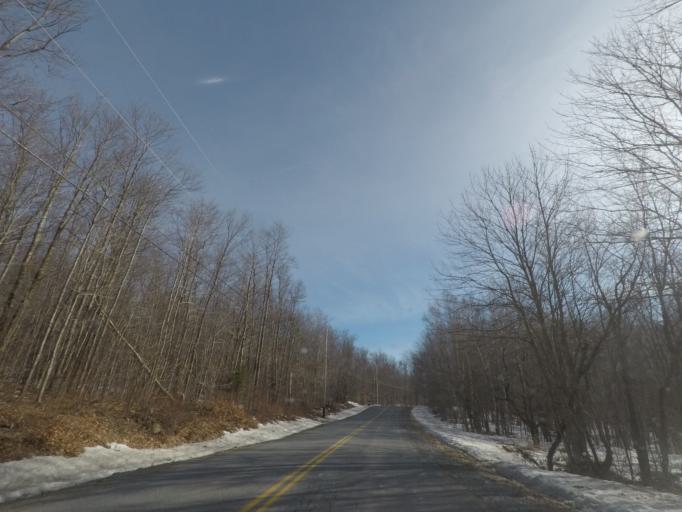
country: US
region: New York
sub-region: Rensselaer County
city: Poestenkill
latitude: 42.7152
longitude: -73.4203
